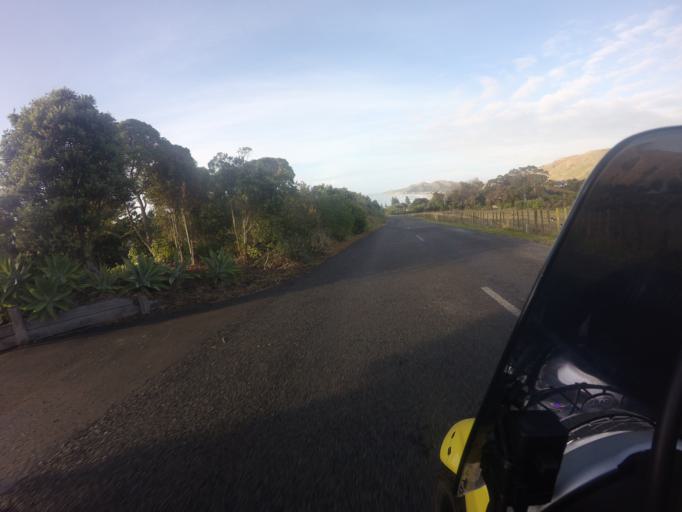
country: NZ
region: Gisborne
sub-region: Gisborne District
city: Gisborne
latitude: -38.6711
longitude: 178.0857
